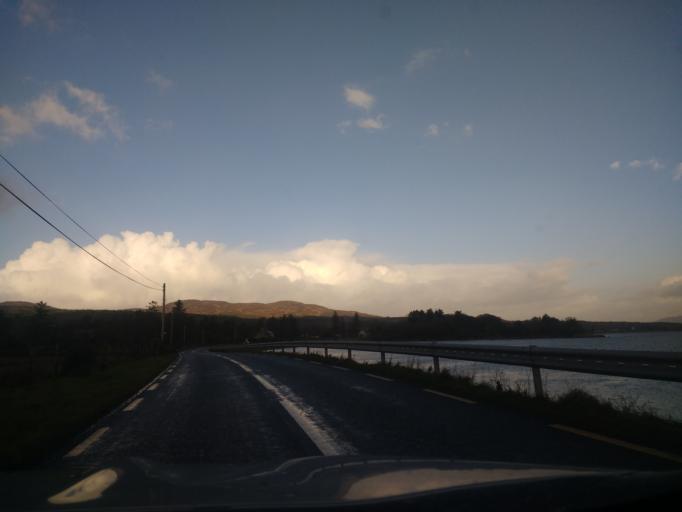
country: IE
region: Ulster
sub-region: County Donegal
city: Ramelton
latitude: 55.0701
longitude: -7.5990
